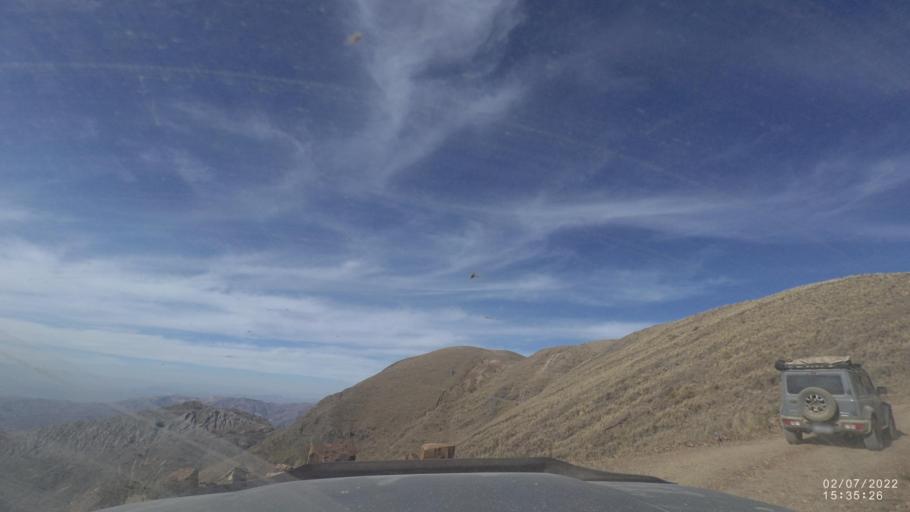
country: BO
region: Cochabamba
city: Irpa Irpa
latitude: -17.8882
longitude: -66.4111
